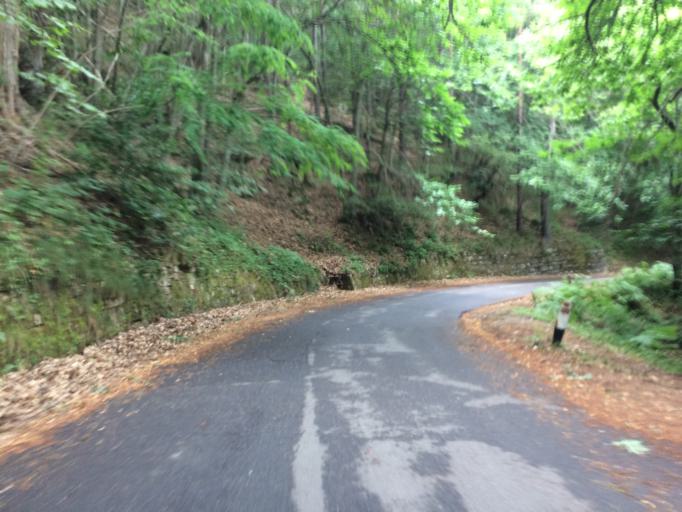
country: IT
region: Liguria
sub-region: Provincia di Imperia
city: Bajardo
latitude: 43.8872
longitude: 7.7333
